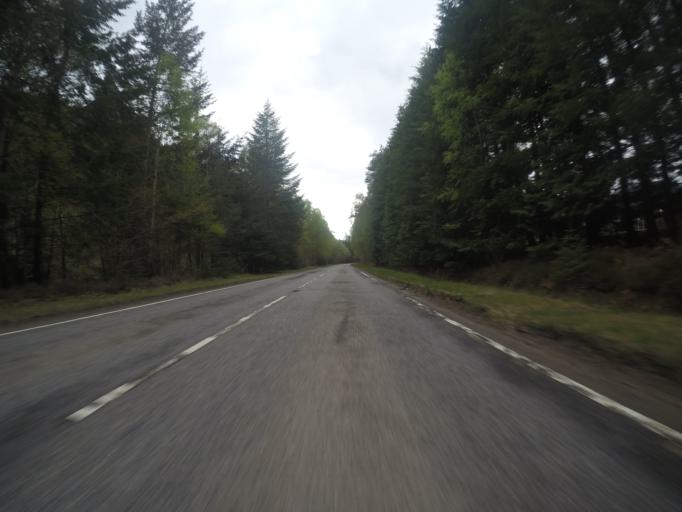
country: GB
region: Scotland
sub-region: Highland
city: Beauly
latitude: 57.2123
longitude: -4.6755
